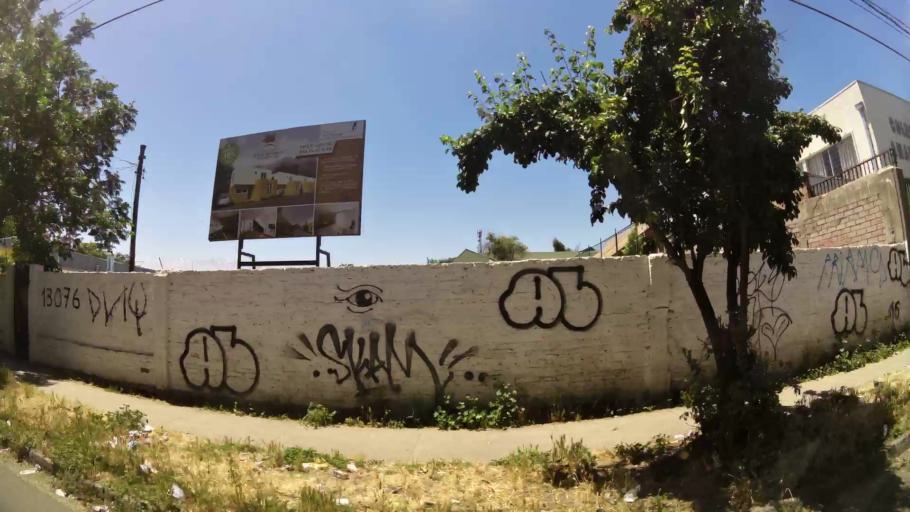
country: CL
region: Santiago Metropolitan
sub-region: Provincia de Santiago
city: La Pintana
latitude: -33.5747
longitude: -70.6630
